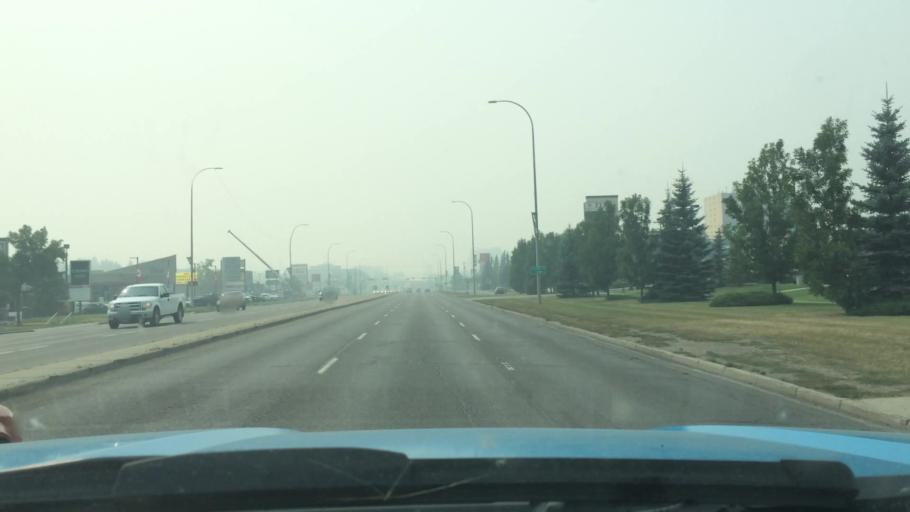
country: CA
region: Alberta
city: Calgary
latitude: 50.9892
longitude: -114.0717
